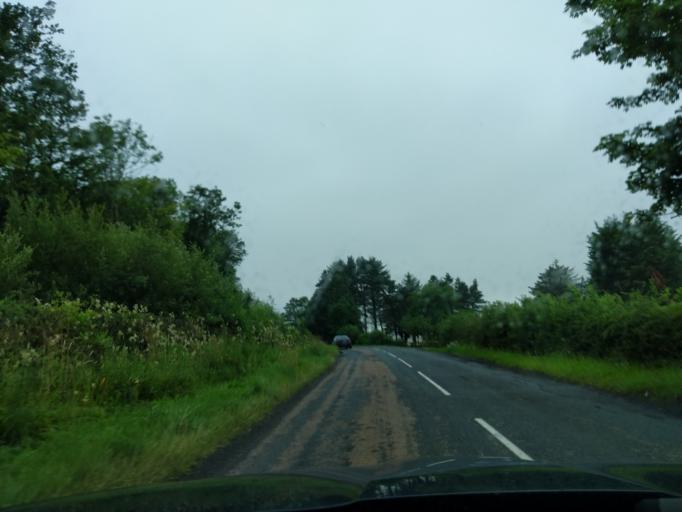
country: GB
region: England
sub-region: Northumberland
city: Lowick
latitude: 55.6598
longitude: -1.9370
